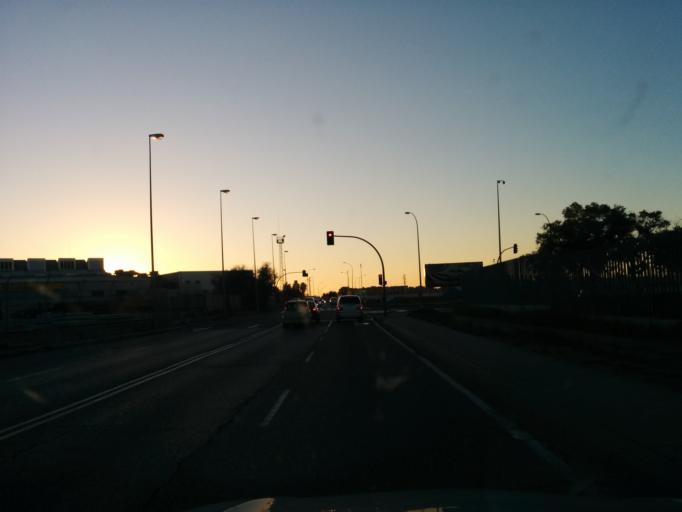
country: ES
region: Andalusia
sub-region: Provincia de Sevilla
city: Sevilla
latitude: 37.3799
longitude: -5.9368
